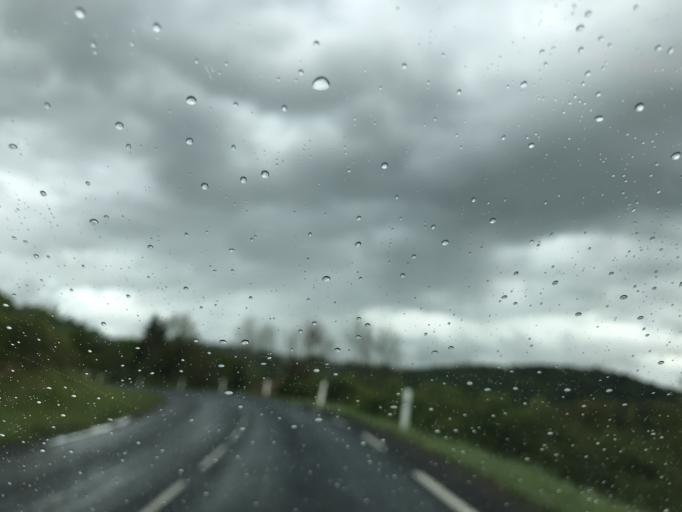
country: FR
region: Auvergne
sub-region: Departement du Puy-de-Dome
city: Billom
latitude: 45.7062
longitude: 3.4107
